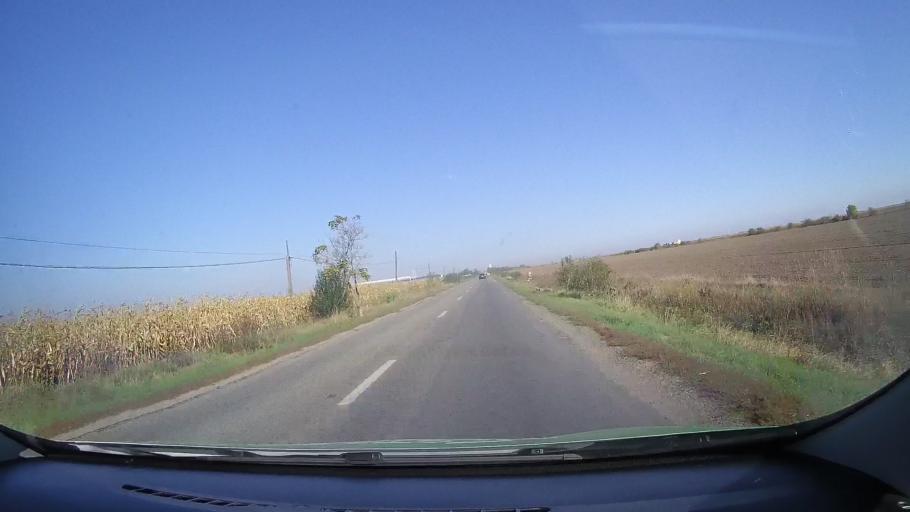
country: RO
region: Satu Mare
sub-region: Oras Tasnad
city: Tasnad
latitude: 47.5007
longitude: 22.5746
